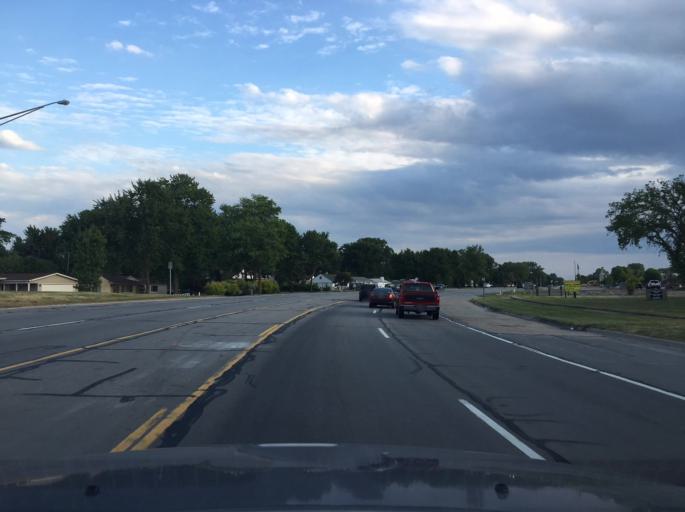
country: US
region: Michigan
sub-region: Macomb County
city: Clinton
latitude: 42.5830
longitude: -82.9022
